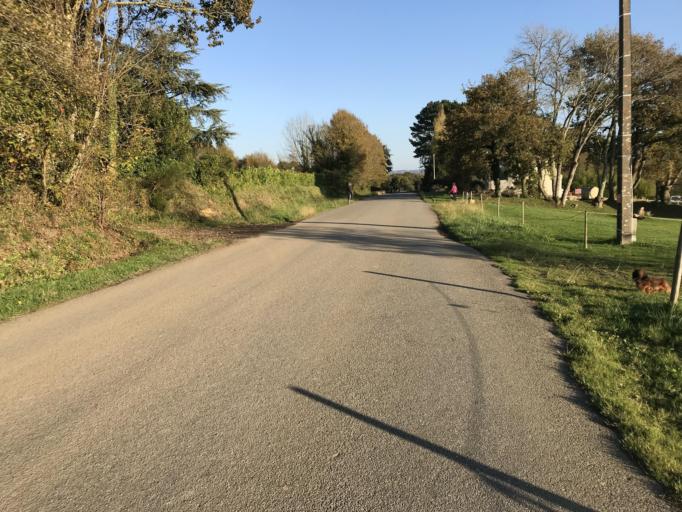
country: FR
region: Brittany
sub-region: Departement du Finistere
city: Le Faou
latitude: 48.2990
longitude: -4.2065
